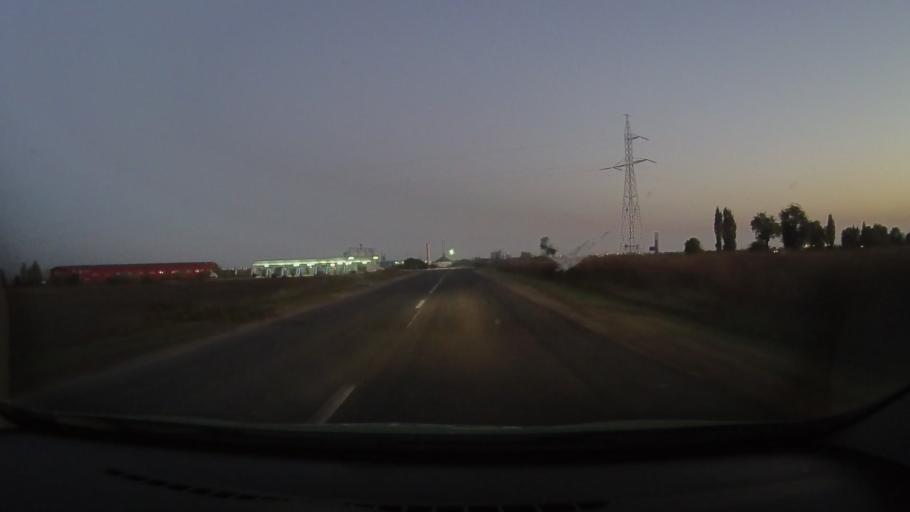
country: RO
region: Arad
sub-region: Comuna Vladimirescu
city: Vladimirescu
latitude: 46.1904
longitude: 21.3924
